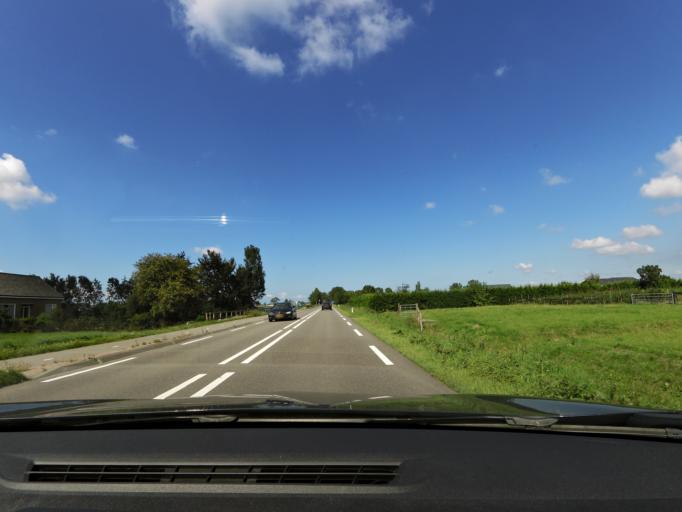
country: NL
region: South Holland
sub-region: Gemeente Nieuwkoop
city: Nieuwkoop
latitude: 52.2037
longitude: 4.7821
